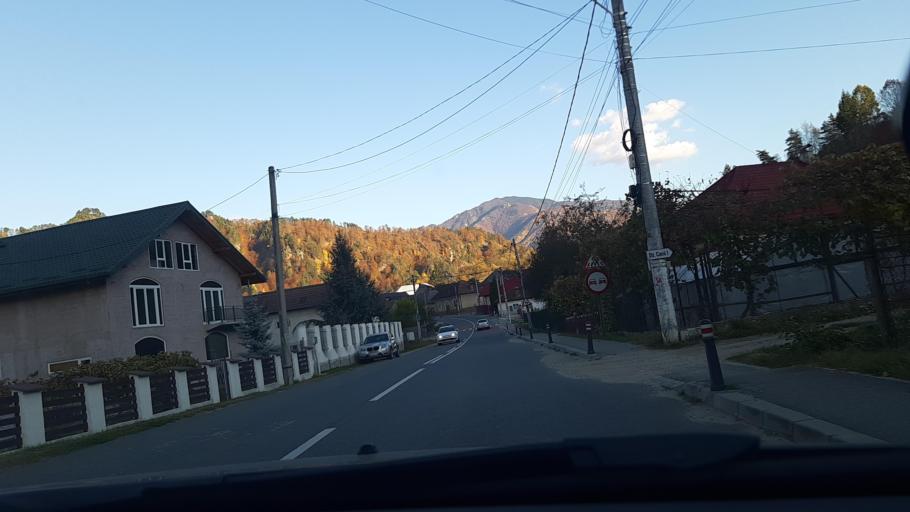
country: RO
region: Valcea
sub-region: Comuna Brezoi
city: Brezoi
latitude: 45.3441
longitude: 24.2352
